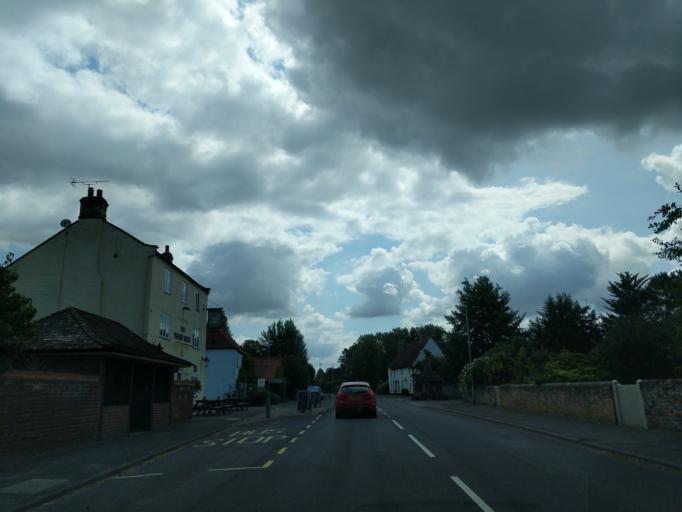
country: GB
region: England
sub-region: Cambridgeshire
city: Isleham
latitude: 52.3024
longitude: 0.4358
